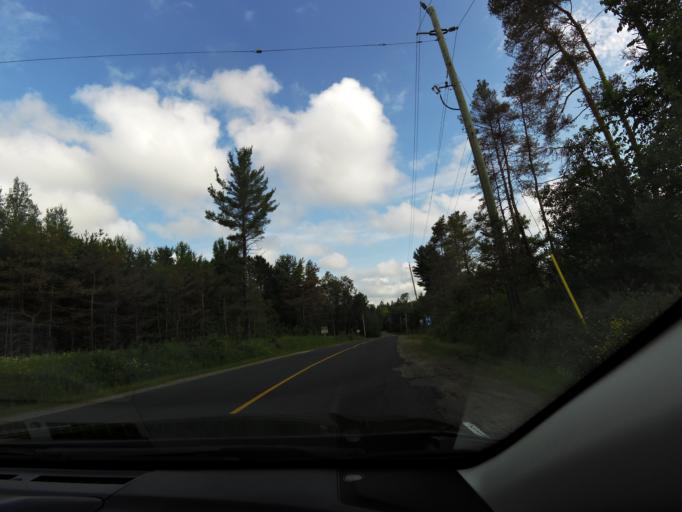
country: CA
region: Ontario
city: Bracebridge
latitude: 45.0334
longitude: -79.3031
